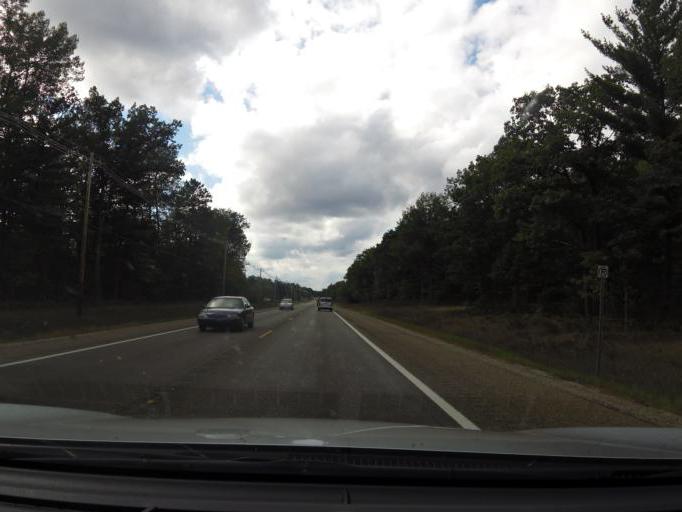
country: US
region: Michigan
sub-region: Roscommon County
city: Prudenville
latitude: 44.3056
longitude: -84.6249
